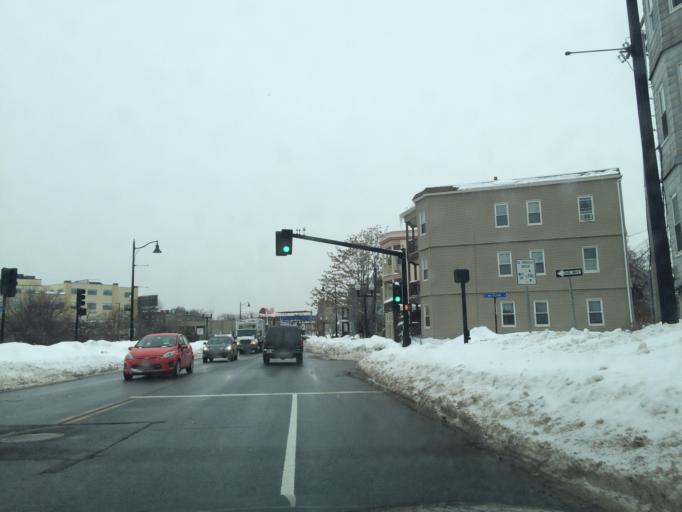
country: US
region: Massachusetts
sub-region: Middlesex County
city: Cambridge
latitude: 42.3871
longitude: -71.1164
